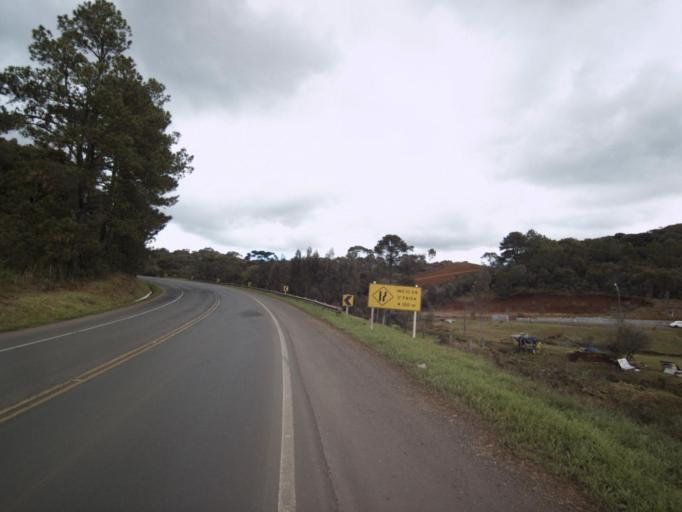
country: BR
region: Santa Catarina
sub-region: Joacaba
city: Joacaba
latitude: -27.0803
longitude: -51.6641
